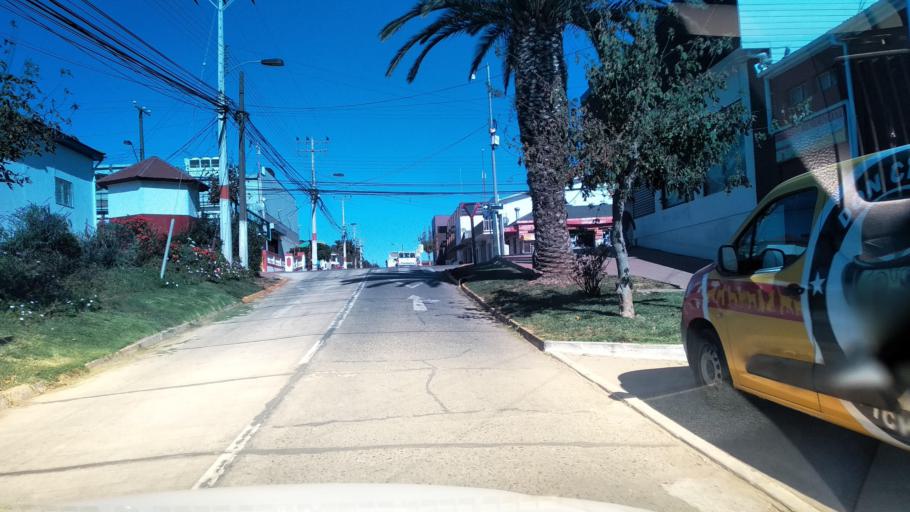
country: CL
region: O'Higgins
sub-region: Provincia de Colchagua
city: Santa Cruz
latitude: -34.3864
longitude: -72.0048
